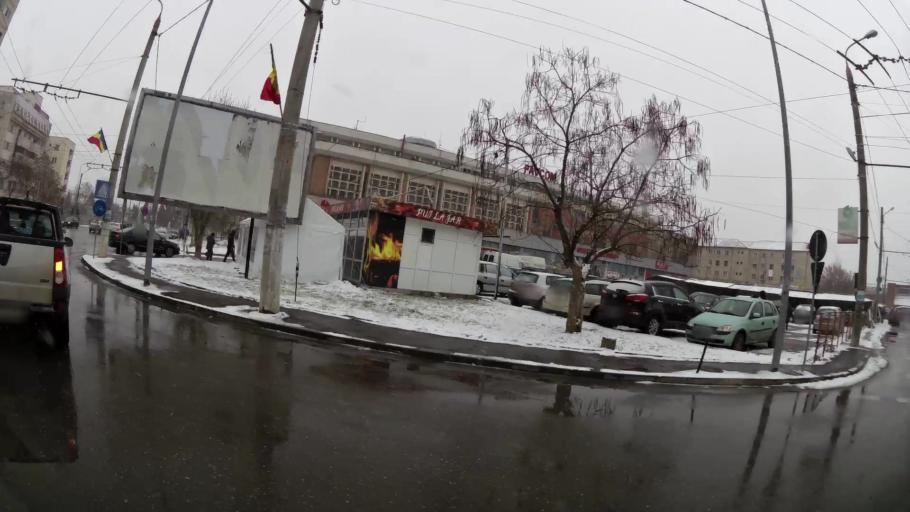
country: RO
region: Dambovita
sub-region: Municipiul Targoviste
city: Targoviste
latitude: 44.9200
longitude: 25.4506
